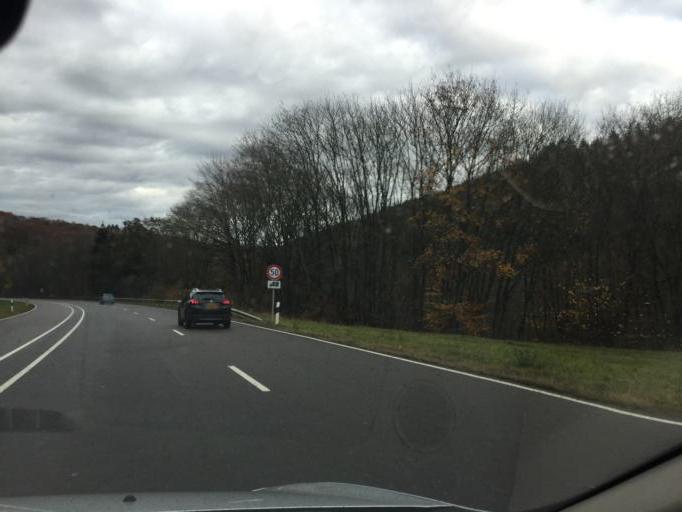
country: LU
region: Diekirch
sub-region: Canton de Wiltz
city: Esch-sur-Sure
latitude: 49.8943
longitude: 5.9530
